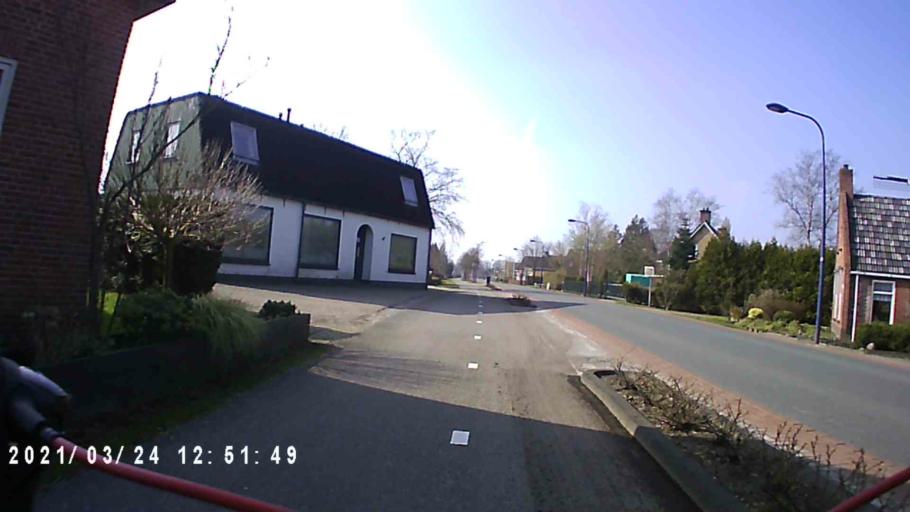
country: NL
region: Groningen
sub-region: Gemeente Leek
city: Leek
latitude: 53.1605
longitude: 6.3255
